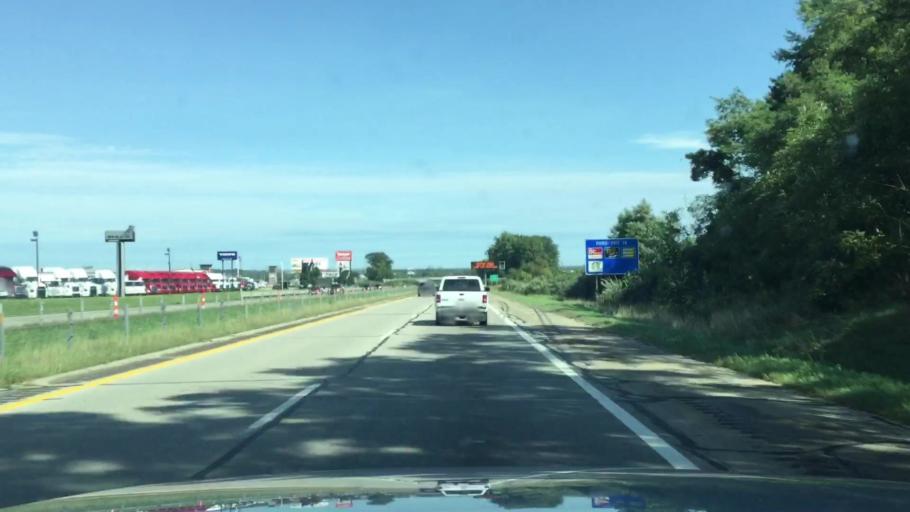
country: US
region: Michigan
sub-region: Kent County
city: Cutlerville
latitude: 42.8041
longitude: -85.6686
